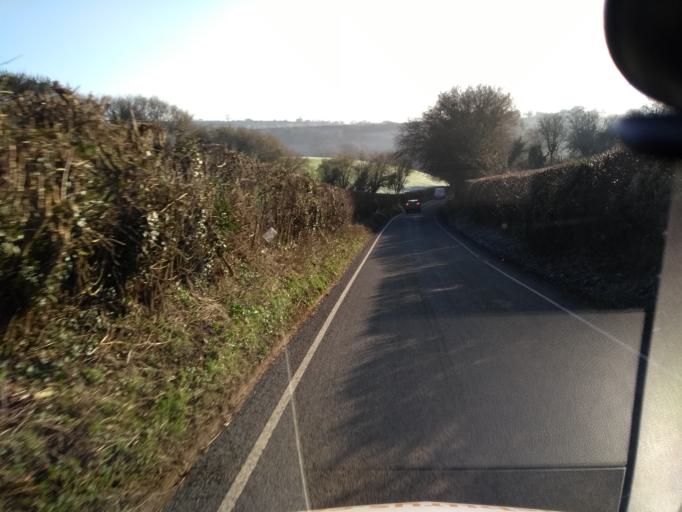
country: GB
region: England
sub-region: Somerset
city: Bruton
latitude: 51.1228
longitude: -2.4611
